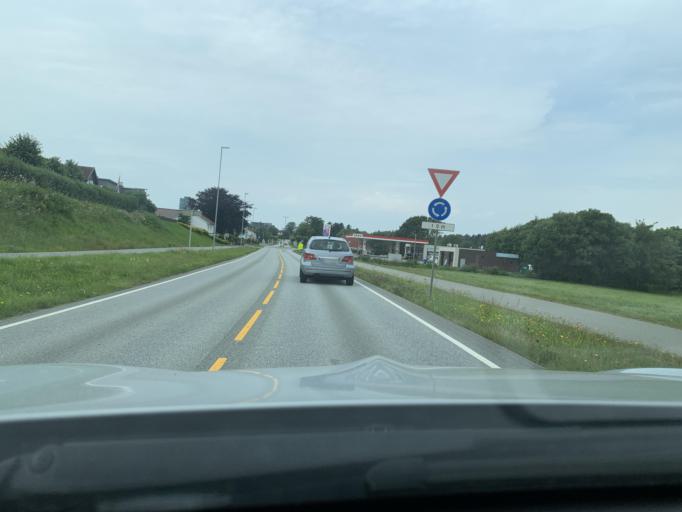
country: NO
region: Rogaland
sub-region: Time
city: Bryne
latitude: 58.7351
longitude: 5.6697
